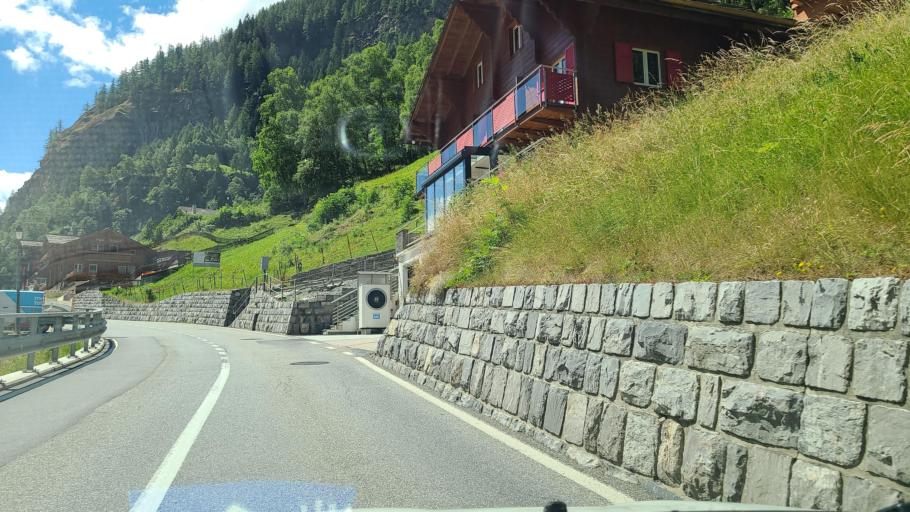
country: CH
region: Valais
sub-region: Visp District
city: Stalden
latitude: 46.1965
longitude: 7.8959
